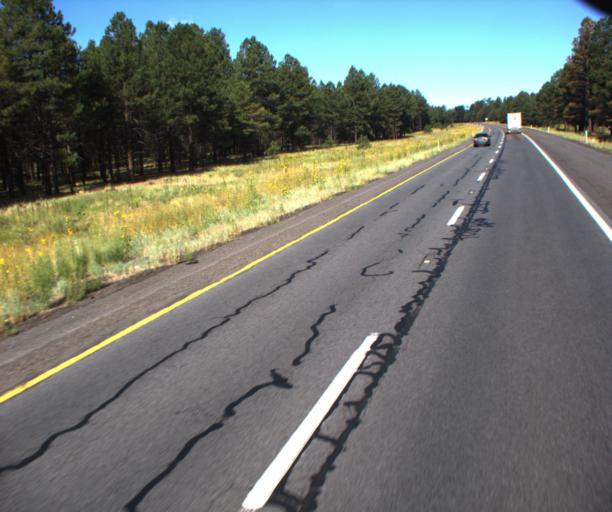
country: US
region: Arizona
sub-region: Coconino County
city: Parks
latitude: 35.2480
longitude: -111.8493
